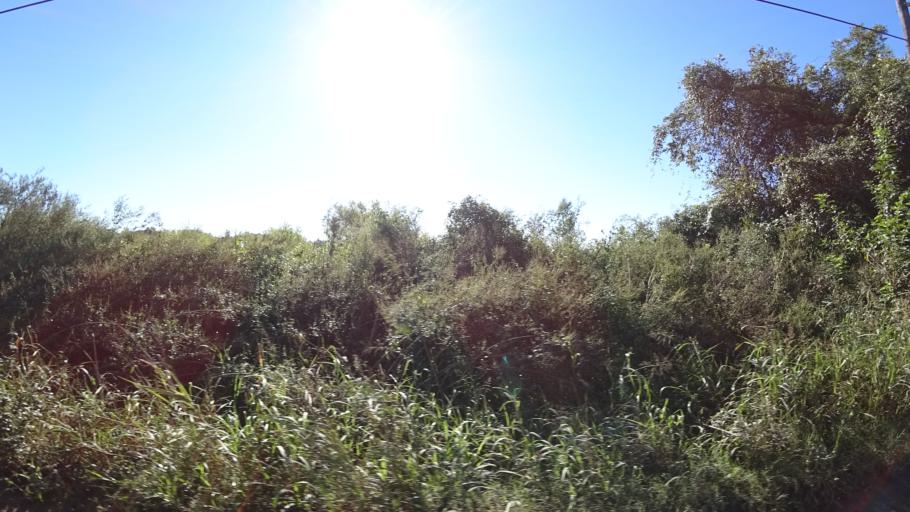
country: US
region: Texas
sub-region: Travis County
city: Hornsby Bend
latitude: 30.2368
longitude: -97.6594
